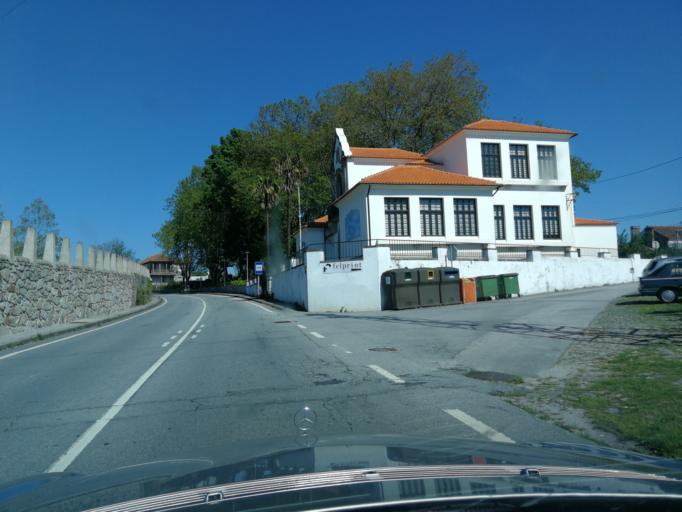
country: PT
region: Viana do Castelo
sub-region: Viana do Castelo
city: Meadela
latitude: 41.7078
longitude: -8.7797
